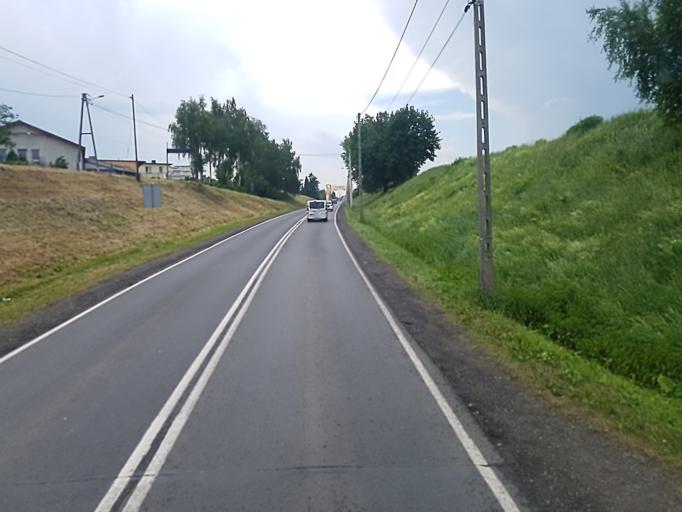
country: PL
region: Silesian Voivodeship
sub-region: Powiat wodzislawski
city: Mszana
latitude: 49.9677
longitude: 18.5437
